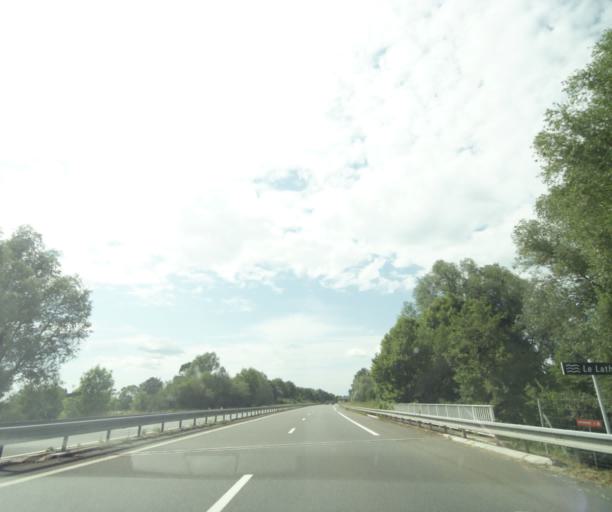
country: FR
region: Pays de la Loire
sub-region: Departement de Maine-et-Loire
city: Jumelles
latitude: 47.3895
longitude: -0.1021
